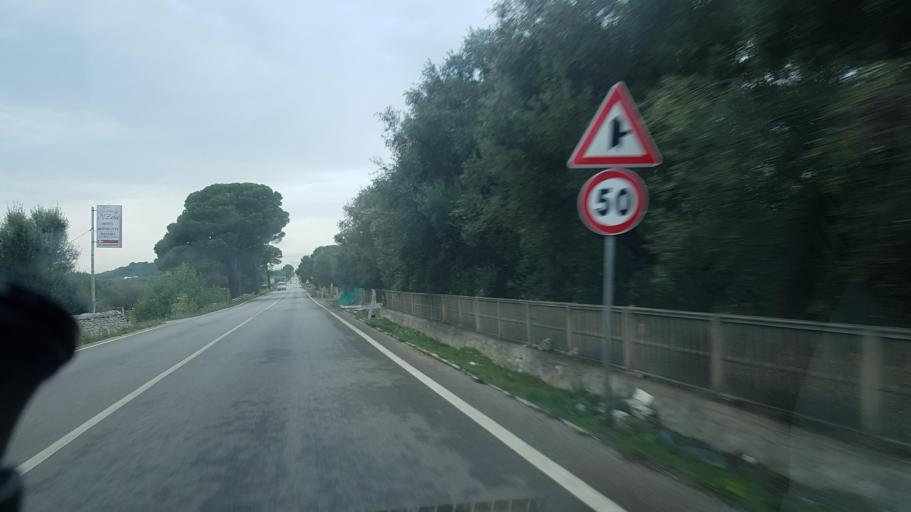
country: IT
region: Apulia
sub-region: Provincia di Brindisi
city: Carovigno
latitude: 40.7123
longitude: 17.6318
